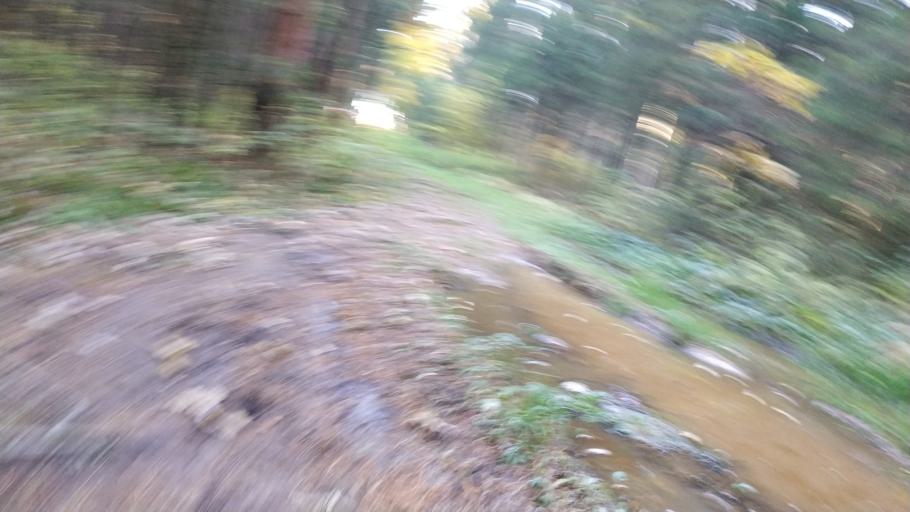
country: RU
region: Moskovskaya
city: Lobnya
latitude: 55.9957
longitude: 37.4667
